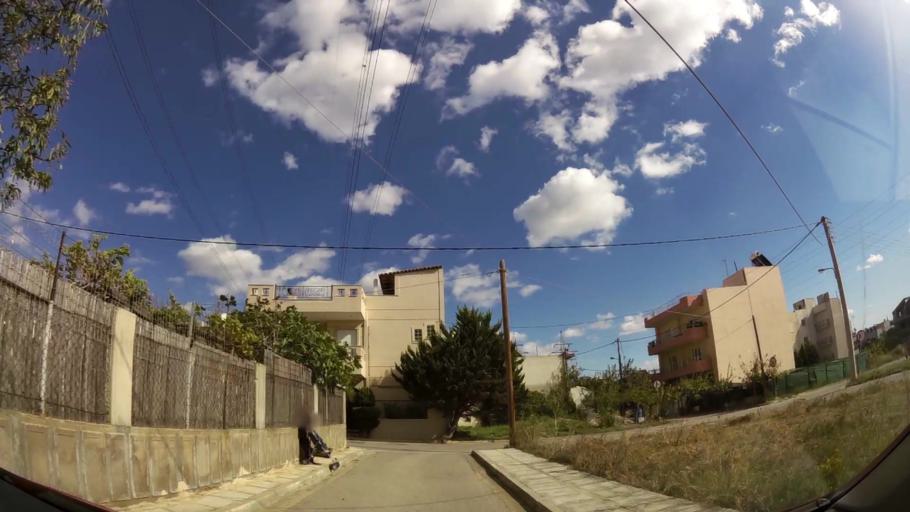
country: GR
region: Attica
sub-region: Nomarchia Anatolikis Attikis
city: Acharnes
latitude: 38.1008
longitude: 23.7305
